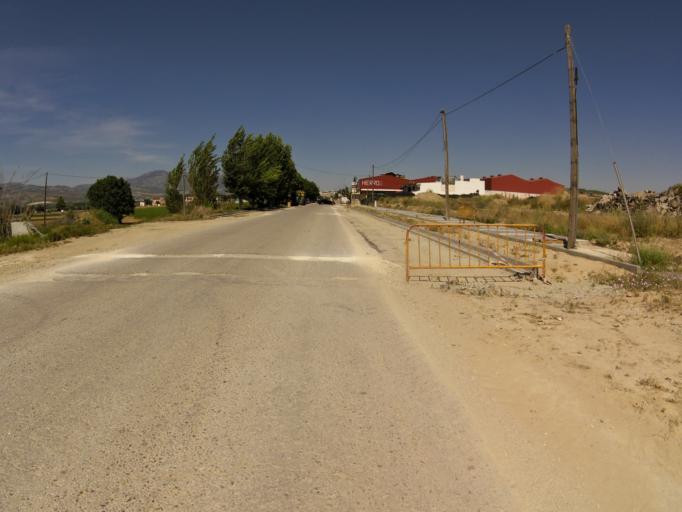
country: ES
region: Andalusia
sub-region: Provincia de Granada
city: Huetor-Tajar
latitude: 37.1837
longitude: -4.0445
